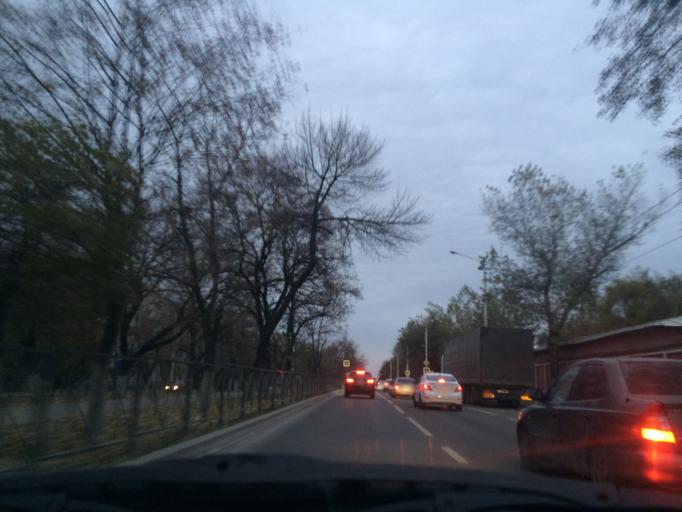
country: RU
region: Rostov
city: Novocherkassk
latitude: 47.4218
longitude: 40.0755
